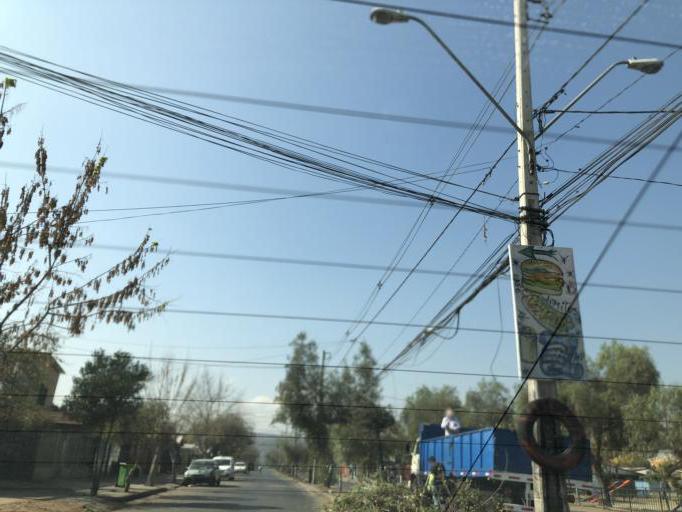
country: CL
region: Santiago Metropolitan
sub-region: Provincia de Cordillera
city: Puente Alto
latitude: -33.6042
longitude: -70.5628
